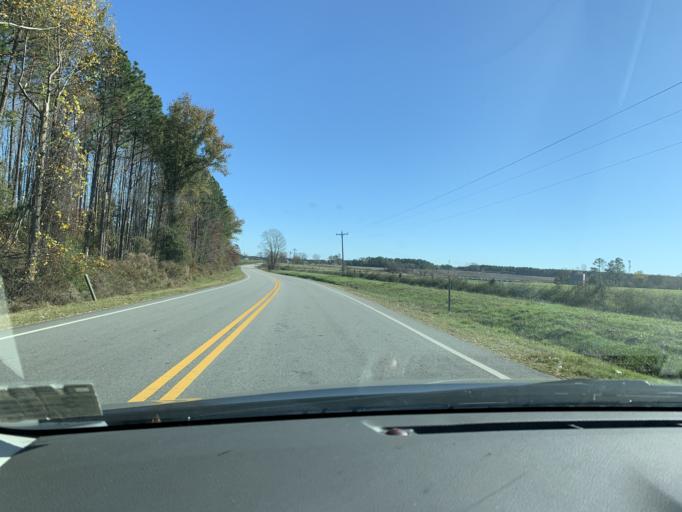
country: US
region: Georgia
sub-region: Ben Hill County
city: Fitzgerald
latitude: 31.7133
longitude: -83.1865
